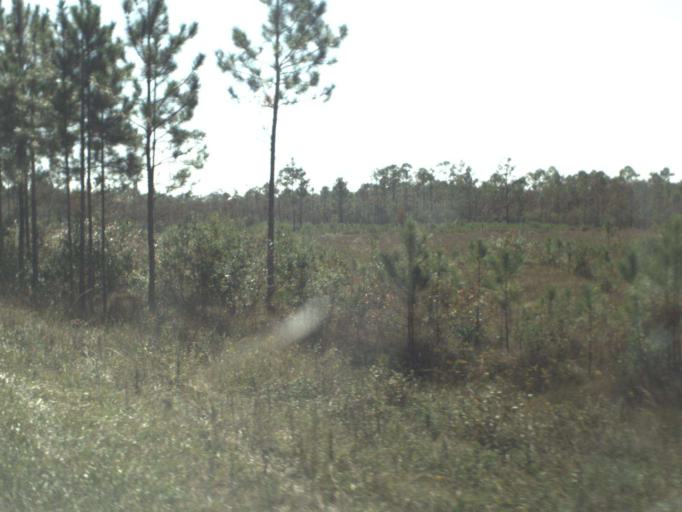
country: US
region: Florida
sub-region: Gulf County
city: Wewahitchka
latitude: 30.0861
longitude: -84.9836
